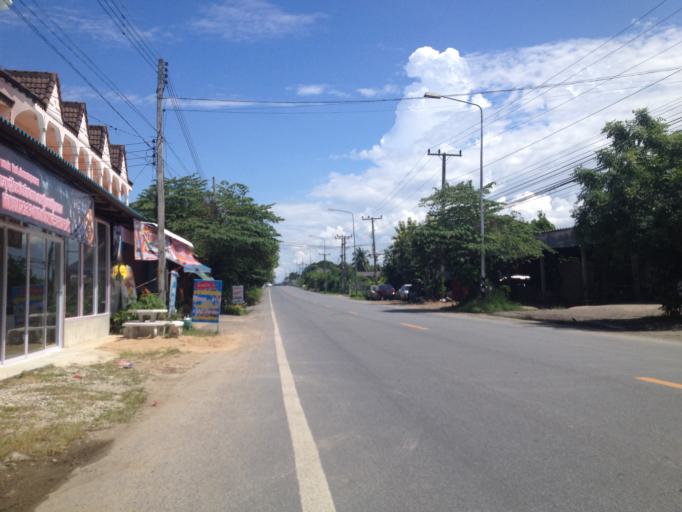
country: TH
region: Lamphun
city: Lamphun
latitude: 18.6009
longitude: 98.9632
